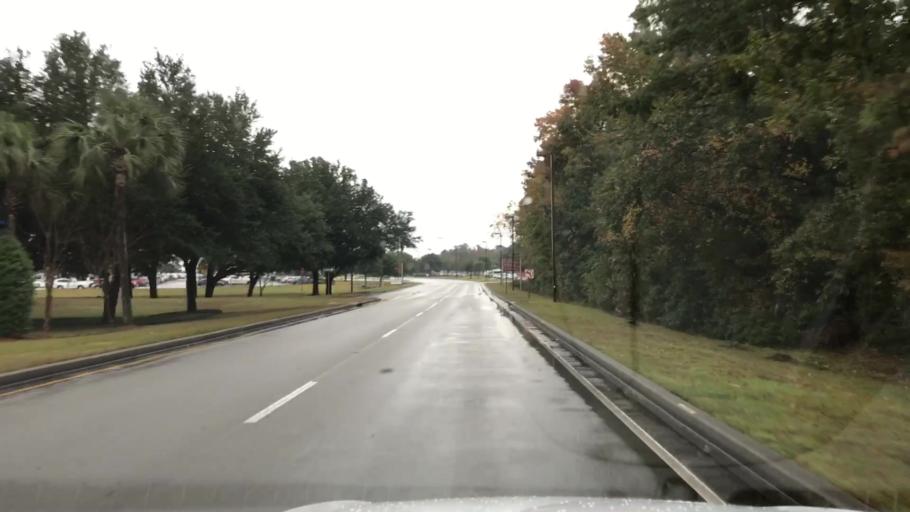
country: US
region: South Carolina
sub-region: Berkeley County
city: Hanahan
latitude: 32.8795
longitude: -80.0356
